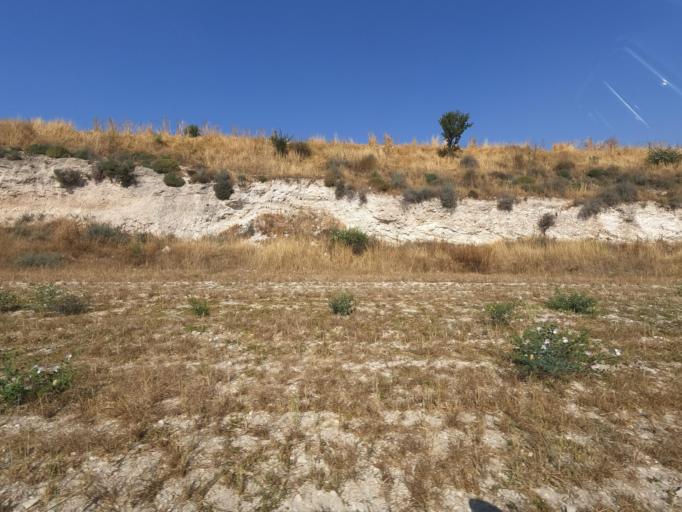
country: CY
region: Lefkosia
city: Lympia
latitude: 34.9795
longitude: 33.4797
